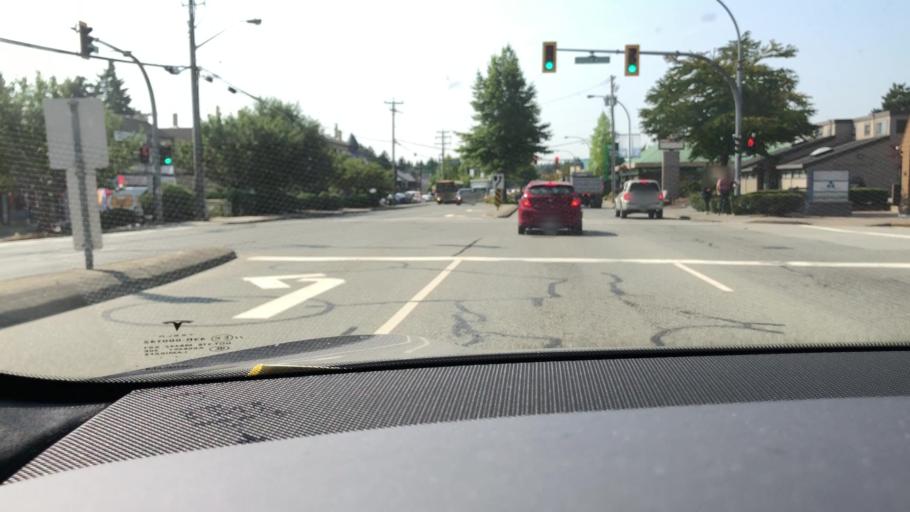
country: US
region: Washington
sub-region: Whatcom County
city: Point Roberts
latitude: 49.0277
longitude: -123.0688
